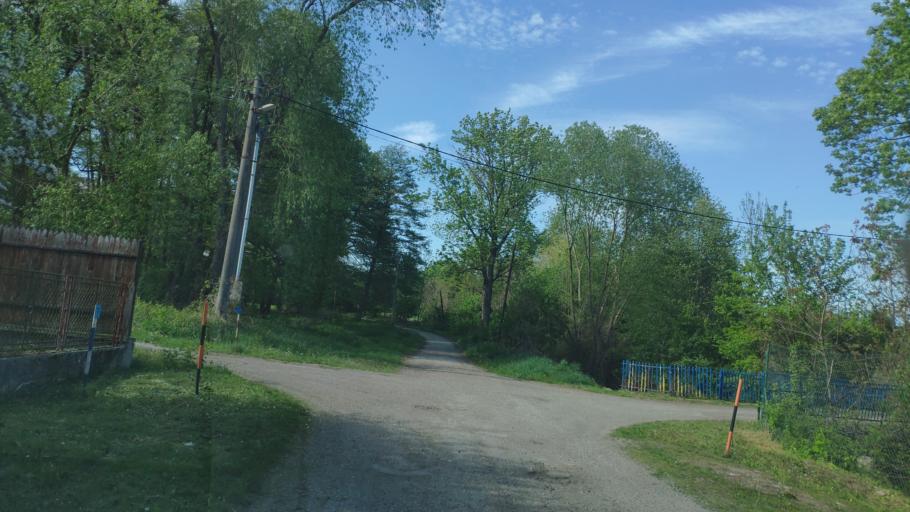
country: SK
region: Kosicky
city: Secovce
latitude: 48.7066
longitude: 21.6156
